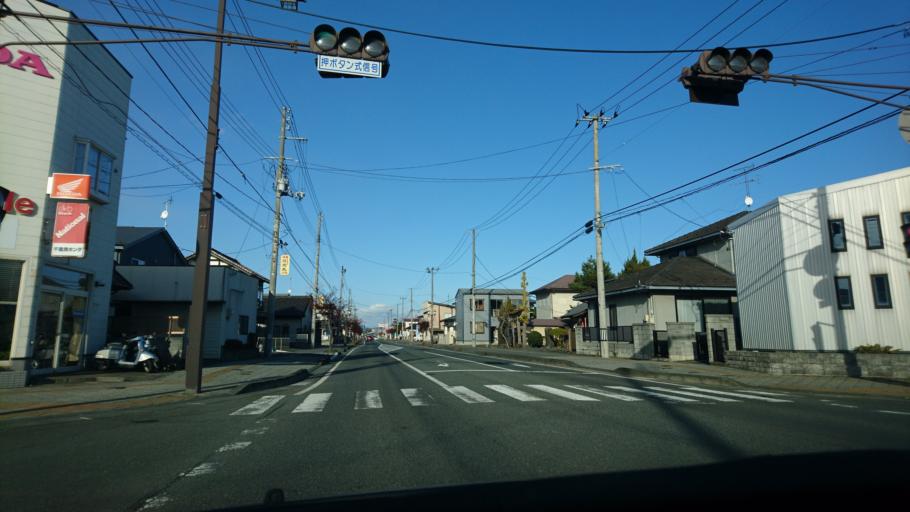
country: JP
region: Iwate
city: Mizusawa
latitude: 39.1491
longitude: 141.1412
